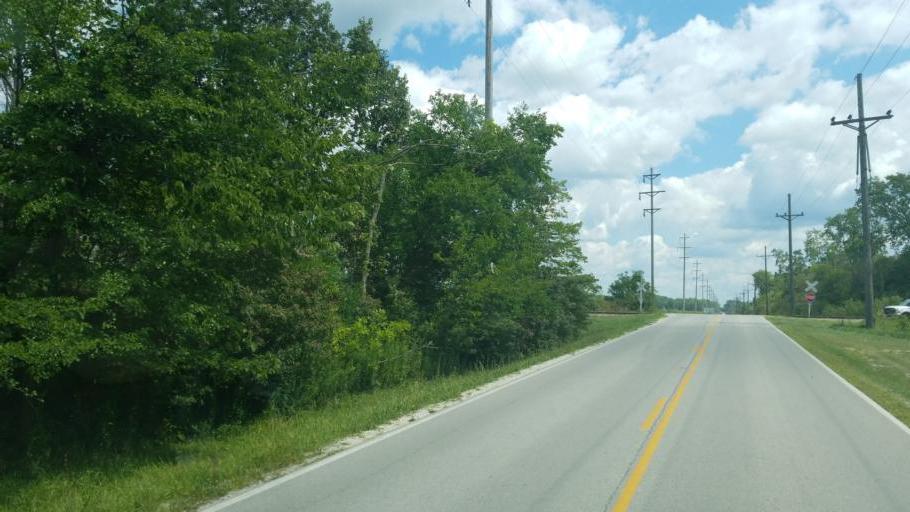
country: US
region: Ohio
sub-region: Sandusky County
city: Gibsonburg
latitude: 41.3990
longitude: -83.3321
